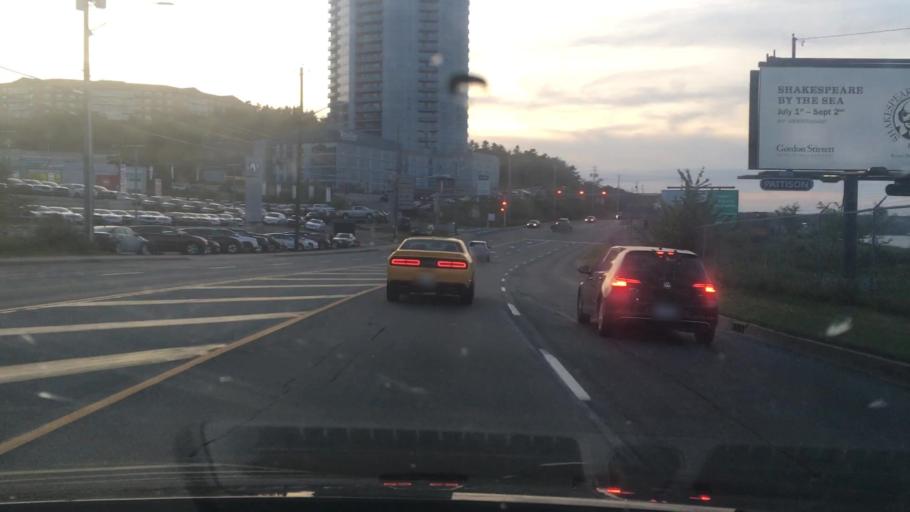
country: CA
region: Nova Scotia
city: Dartmouth
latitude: 44.6636
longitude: -63.6328
